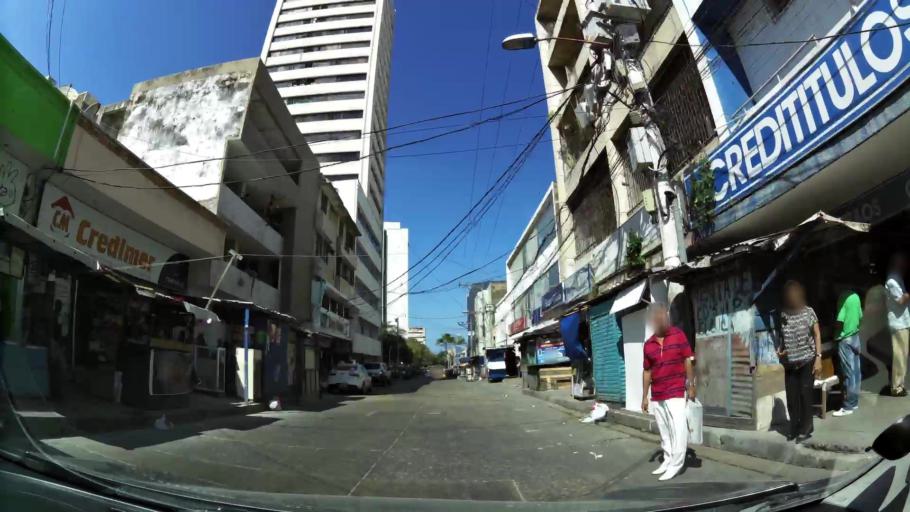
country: CO
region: Atlantico
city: Barranquilla
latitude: 10.9827
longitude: -74.7805
